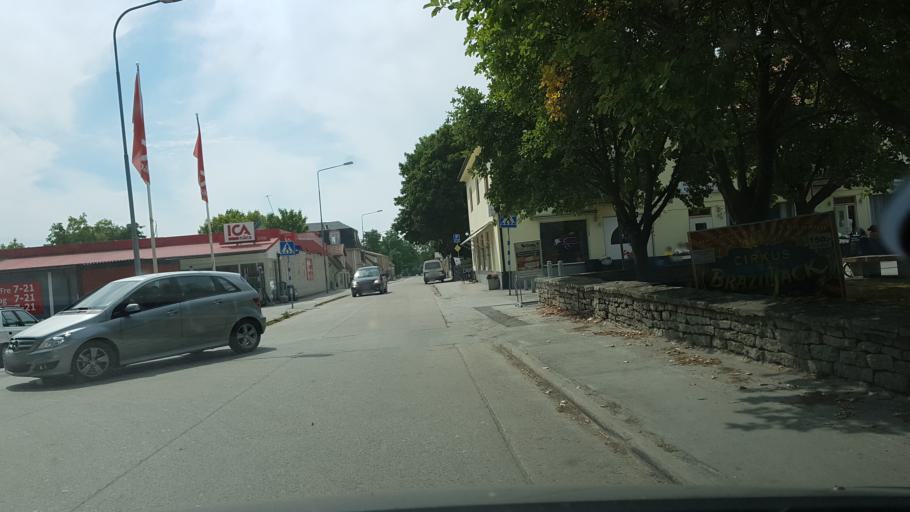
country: SE
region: Gotland
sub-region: Gotland
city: Slite
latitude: 57.7049
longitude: 18.8063
